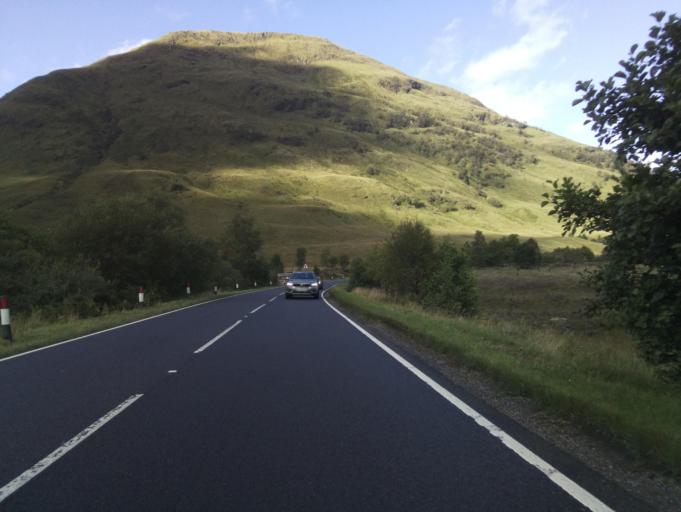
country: GB
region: Scotland
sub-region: Highland
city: Fort William
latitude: 56.6614
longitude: -5.0669
